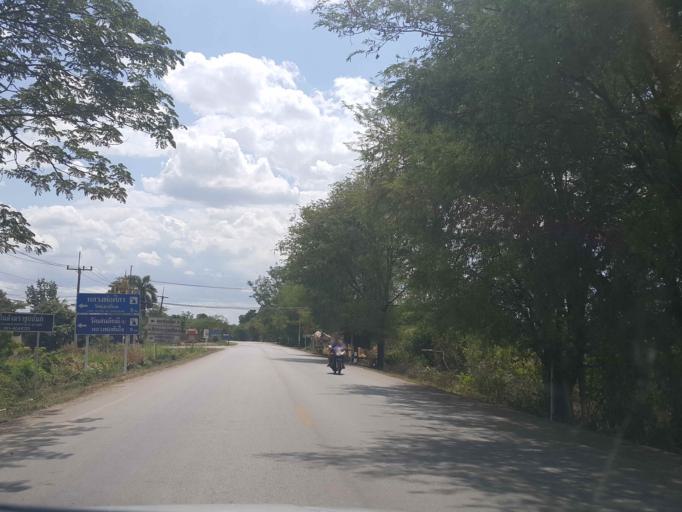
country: TH
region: Sukhothai
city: Thung Saliam
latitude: 17.3370
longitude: 99.5840
